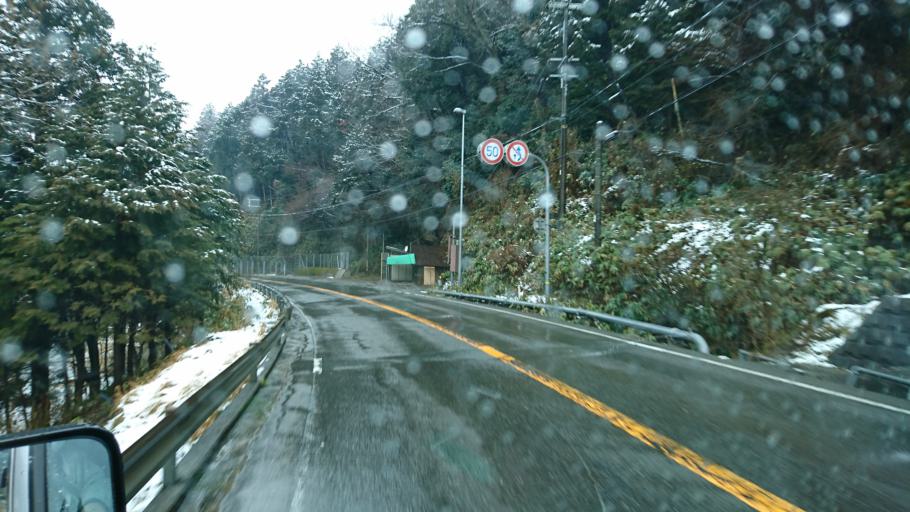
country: JP
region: Tottori
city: Tottori
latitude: 35.5385
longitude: 134.5106
